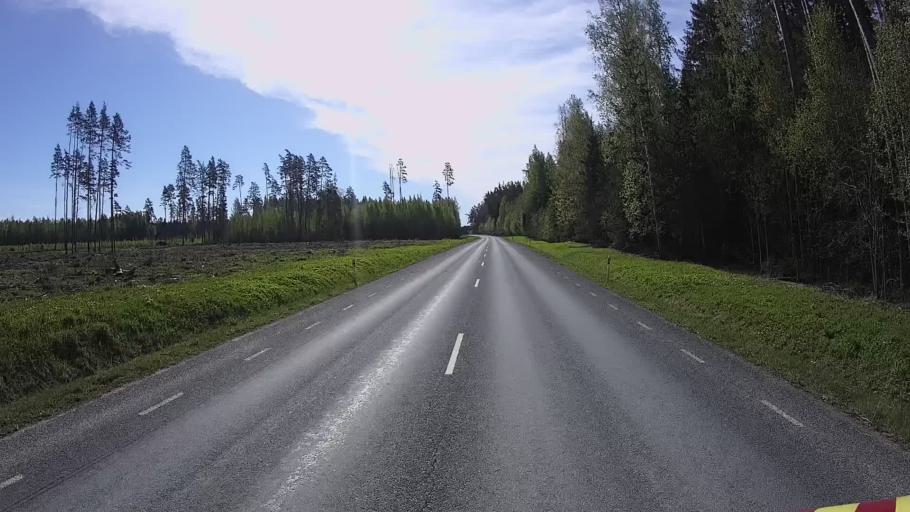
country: EE
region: Polvamaa
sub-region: Polva linn
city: Polva
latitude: 58.1656
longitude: 27.1487
